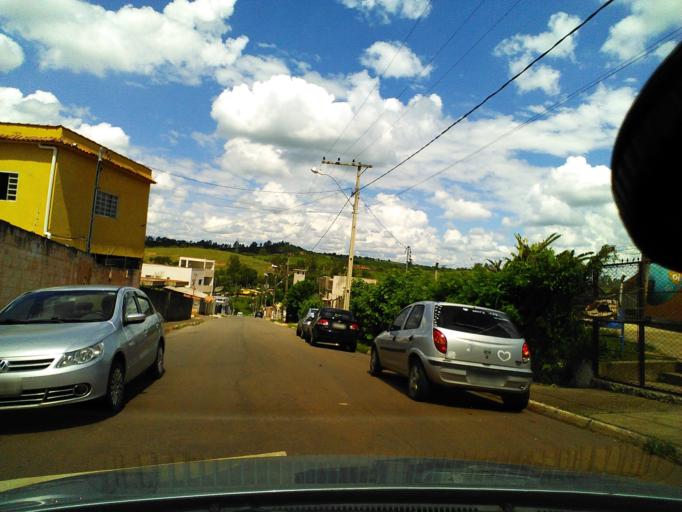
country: BR
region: Minas Gerais
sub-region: Tres Coracoes
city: Tres Coracoes
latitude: -21.7266
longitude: -45.2629
